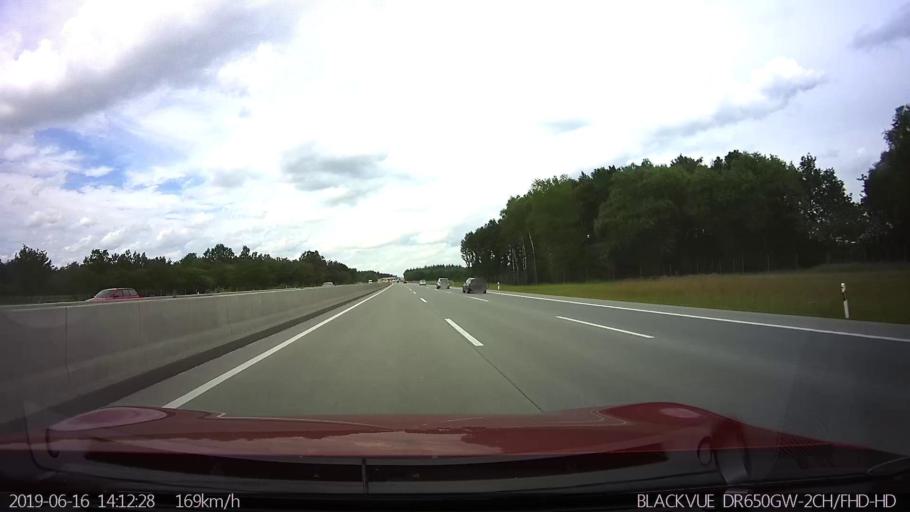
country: DE
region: Schleswig-Holstein
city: Schmalfeld
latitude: 53.8848
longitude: 9.9447
